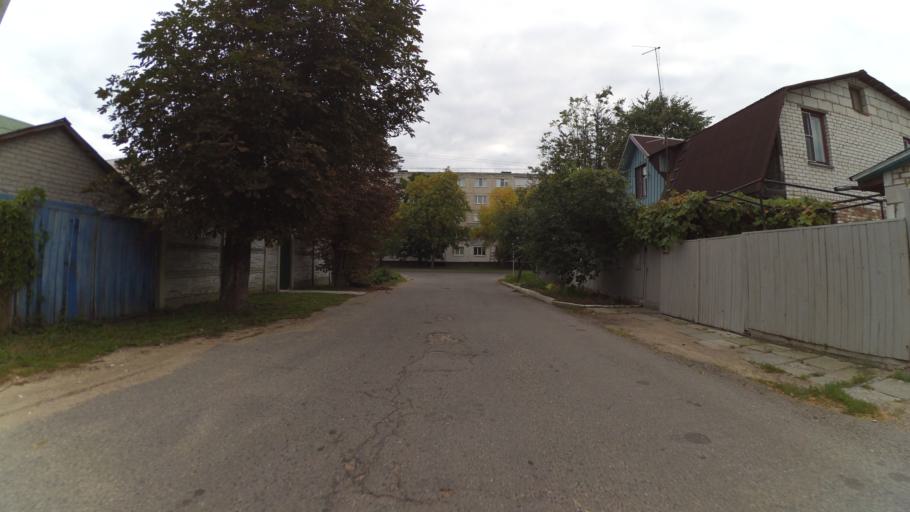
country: BY
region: Minsk
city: Vyaliki Trastsyanets
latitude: 53.8774
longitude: 27.6805
